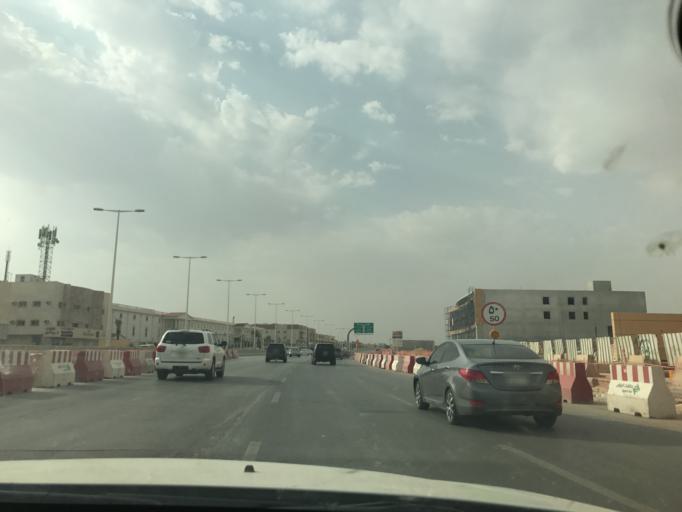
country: SA
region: Ar Riyad
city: Riyadh
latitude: 24.7167
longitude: 46.6959
